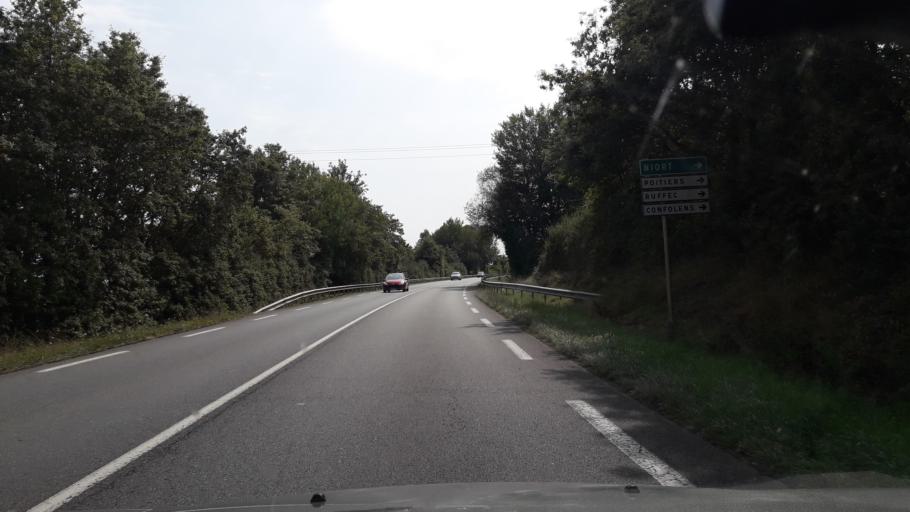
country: FR
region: Poitou-Charentes
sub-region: Departement de la Charente
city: Confolens
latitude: 46.0288
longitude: 0.6584
